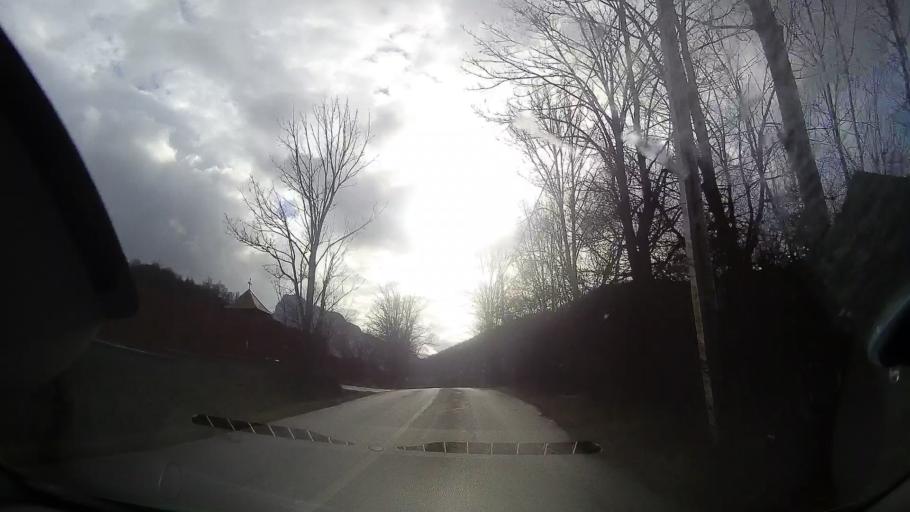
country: RO
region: Alba
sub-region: Comuna Rimetea
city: Rimetea
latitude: 46.4833
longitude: 23.5807
